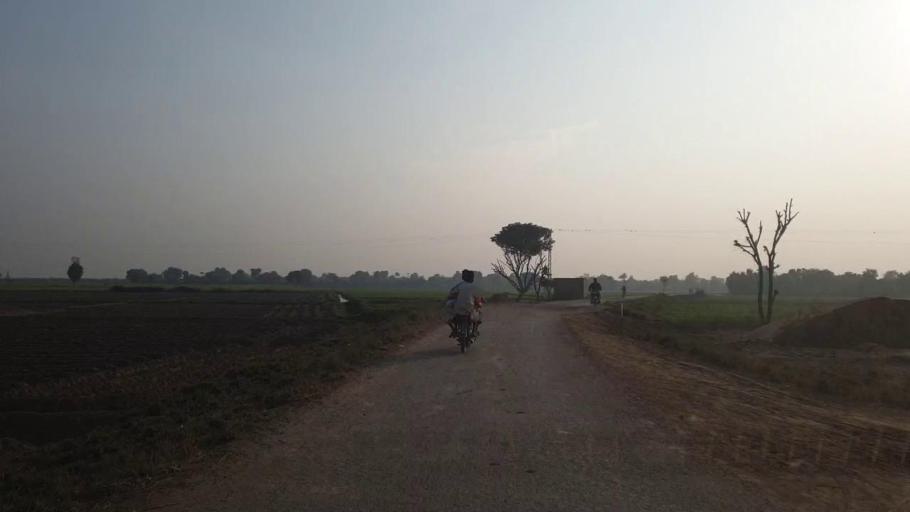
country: PK
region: Sindh
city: Bhit Shah
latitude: 25.8054
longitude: 68.4643
